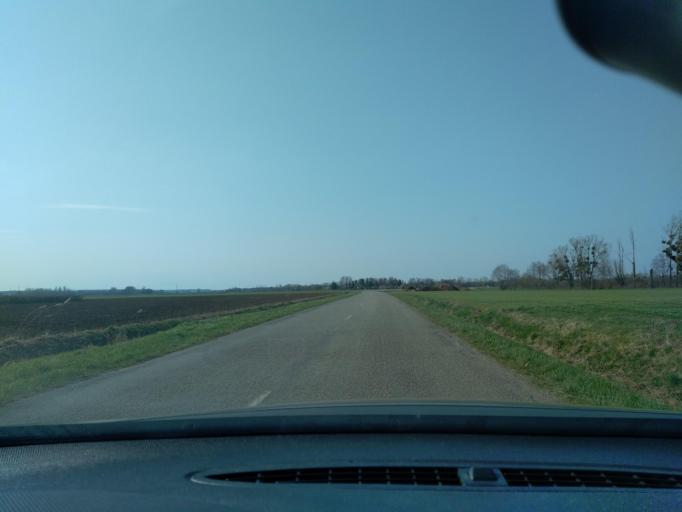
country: FR
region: Franche-Comte
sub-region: Departement du Jura
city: Mont-sous-Vaudrey
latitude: 46.9984
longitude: 5.6030
